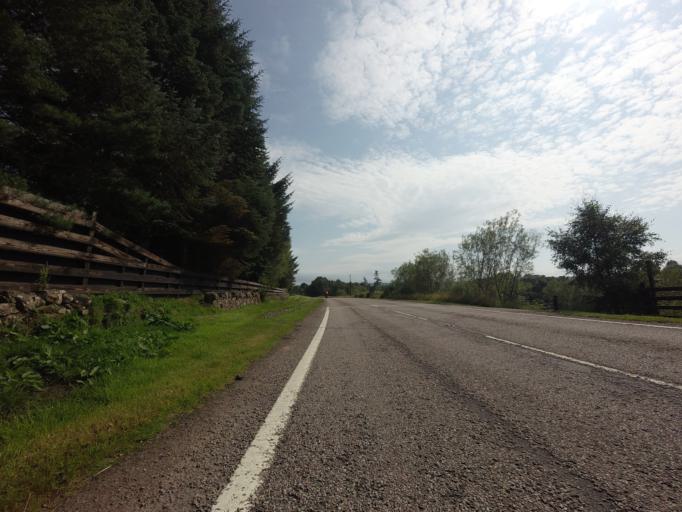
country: GB
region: Scotland
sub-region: Highland
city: Evanton
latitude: 57.9221
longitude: -4.3989
